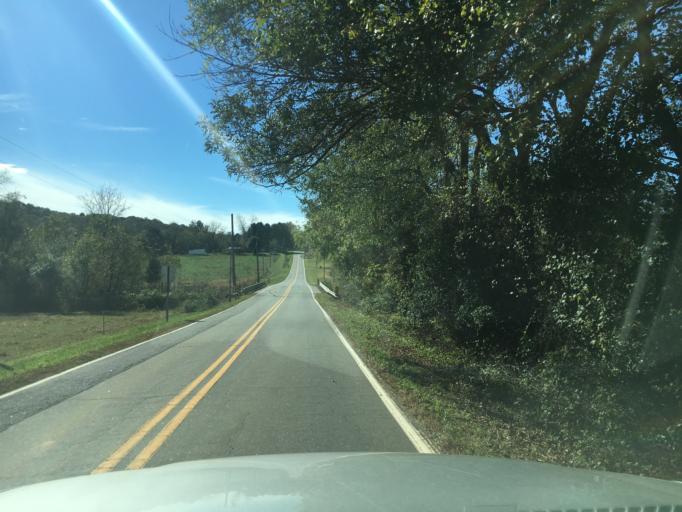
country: US
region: North Carolina
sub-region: Burke County
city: Salem
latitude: 35.7200
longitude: -81.7236
